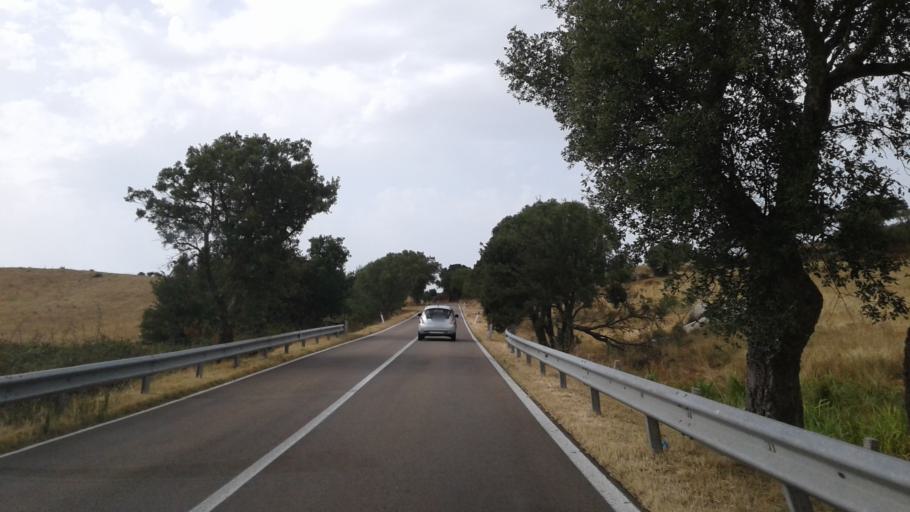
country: IT
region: Sardinia
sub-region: Provincia di Olbia-Tempio
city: Sant'Antonio di Gallura
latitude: 40.9470
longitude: 9.2980
